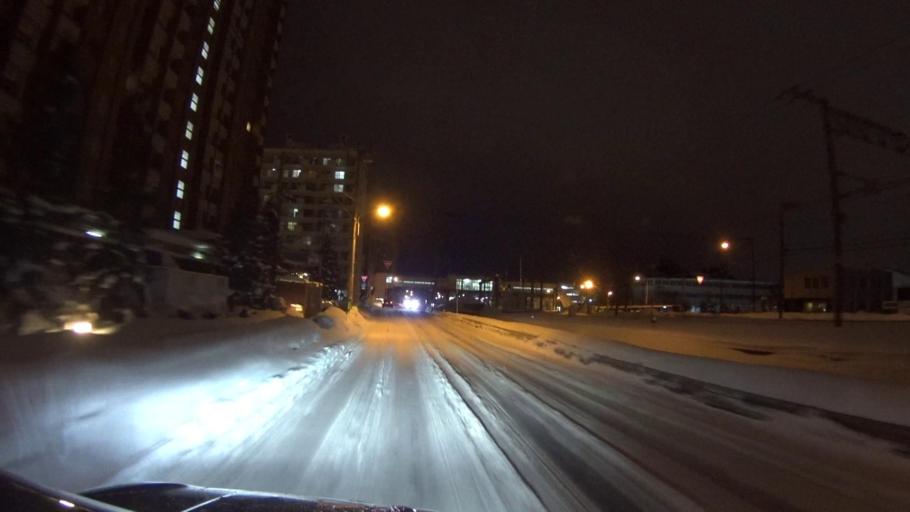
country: JP
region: Hokkaido
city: Sapporo
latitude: 43.0985
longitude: 141.2790
